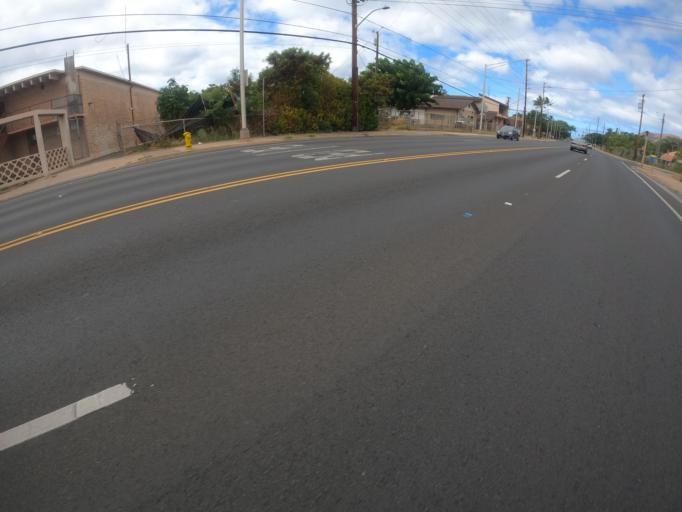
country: US
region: Hawaii
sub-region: Honolulu County
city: Waianae
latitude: 21.4497
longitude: -158.1908
